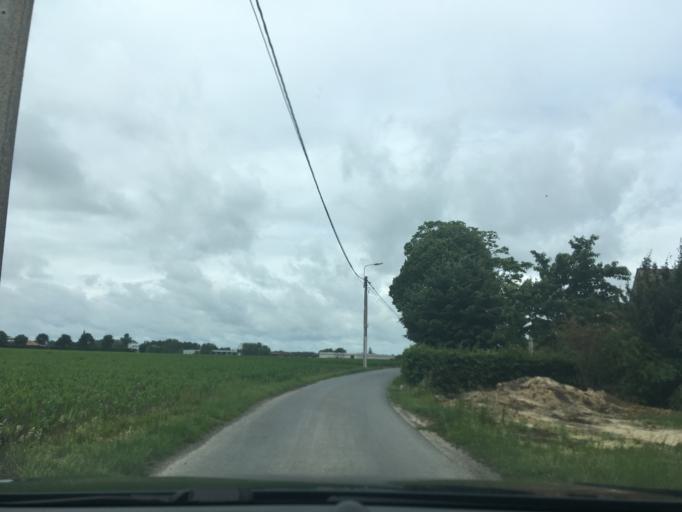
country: BE
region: Flanders
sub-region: Provincie West-Vlaanderen
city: Hooglede
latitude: 50.9478
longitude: 3.0690
